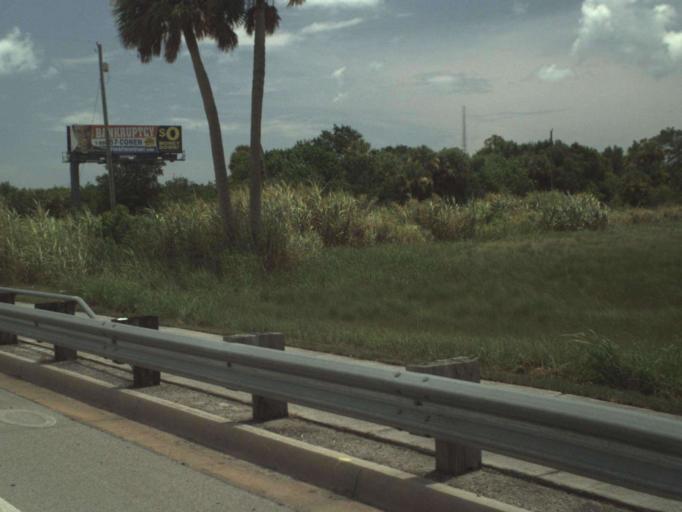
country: US
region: Florida
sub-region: Saint Lucie County
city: Fort Pierce South
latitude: 27.4229
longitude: -80.3717
